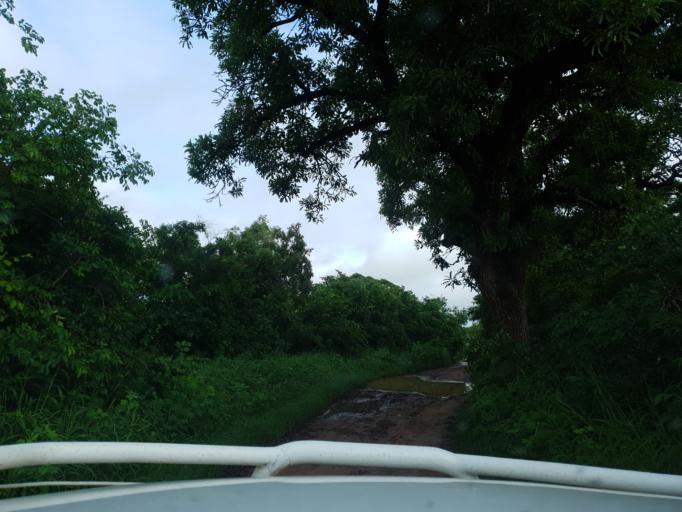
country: ML
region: Segou
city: Baroueli
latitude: 13.3980
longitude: -7.0056
